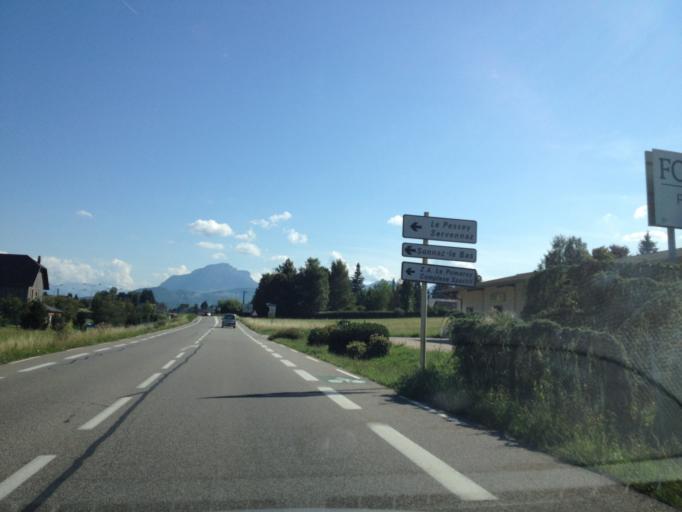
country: FR
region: Rhone-Alpes
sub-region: Departement de la Savoie
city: Sonnaz
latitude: 45.6122
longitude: 5.9104
